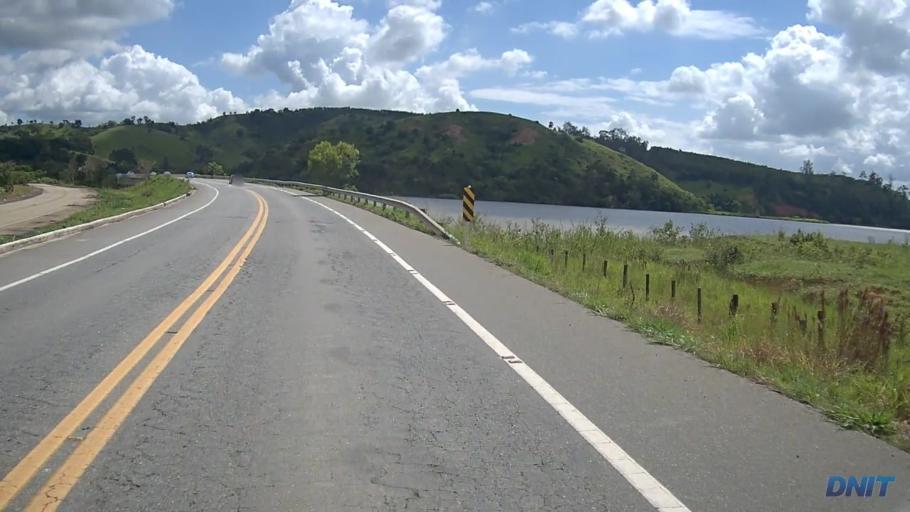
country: BR
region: Minas Gerais
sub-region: Governador Valadares
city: Governador Valadares
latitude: -19.0415
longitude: -42.1492
